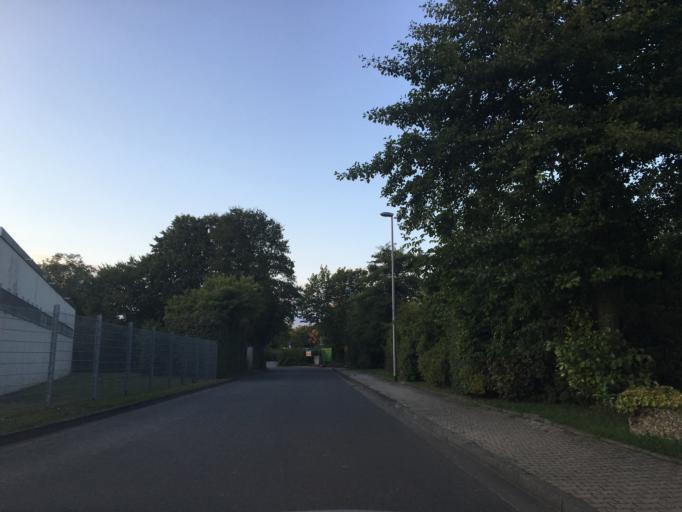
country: DE
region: Hesse
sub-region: Regierungsbezirk Darmstadt
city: Gross-Gerau
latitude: 49.9120
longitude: 8.4808
